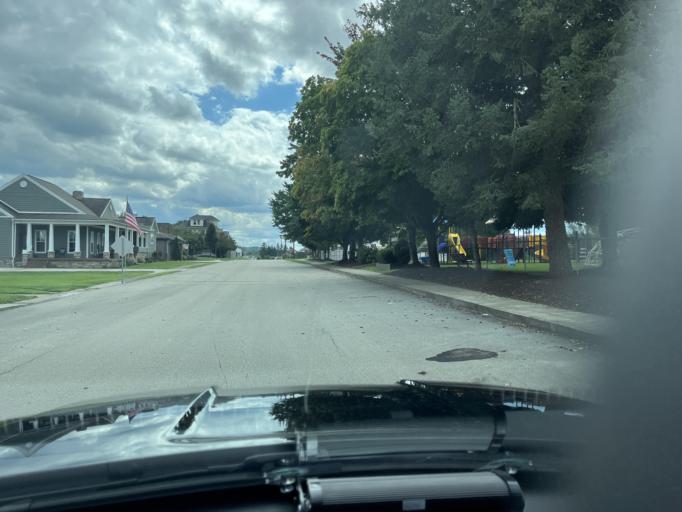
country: US
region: Pennsylvania
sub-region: Fayette County
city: South Uniontown
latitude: 39.8948
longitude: -79.7490
